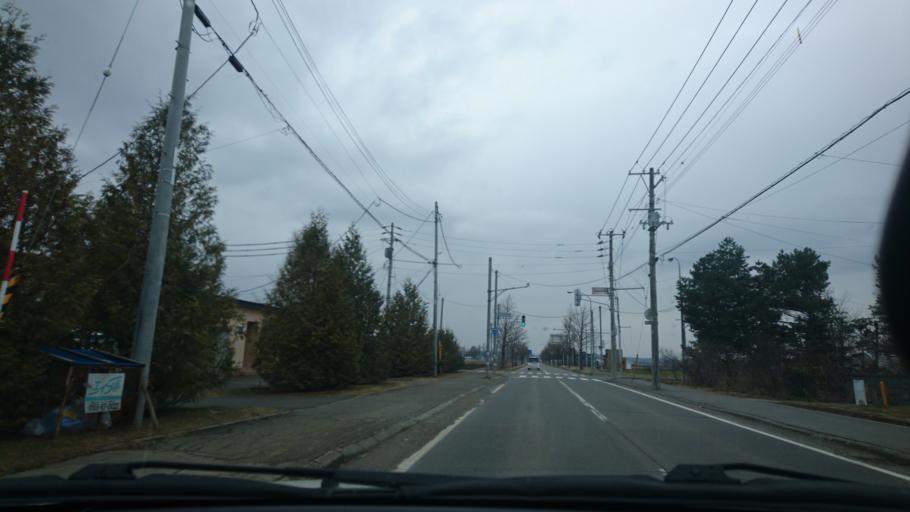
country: JP
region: Hokkaido
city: Otofuke
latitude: 42.9715
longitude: 143.1926
